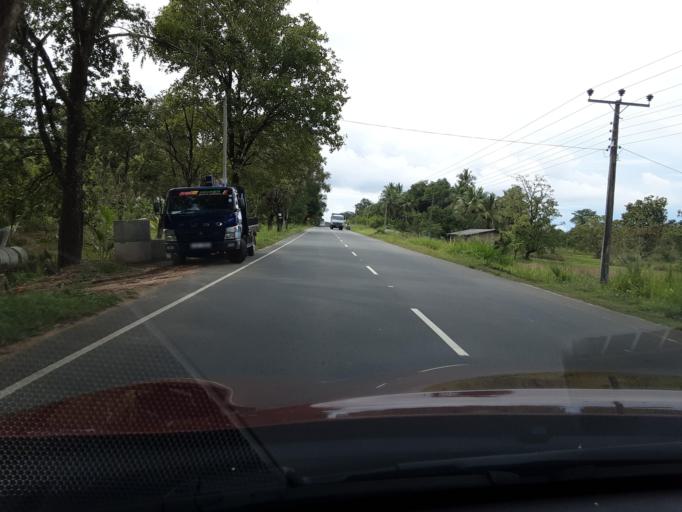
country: LK
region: Uva
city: Badulla
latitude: 7.3932
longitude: 81.1304
